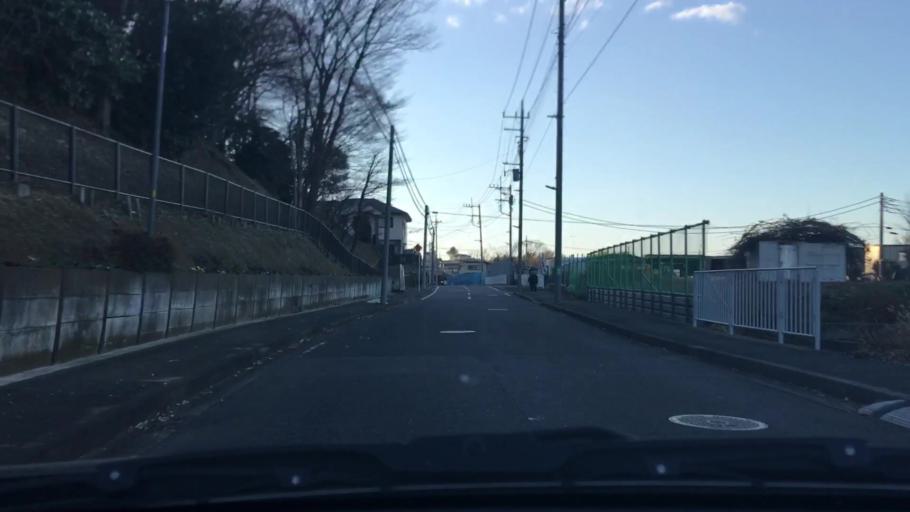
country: JP
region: Tokyo
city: Chofugaoka
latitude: 35.5506
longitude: 139.5718
